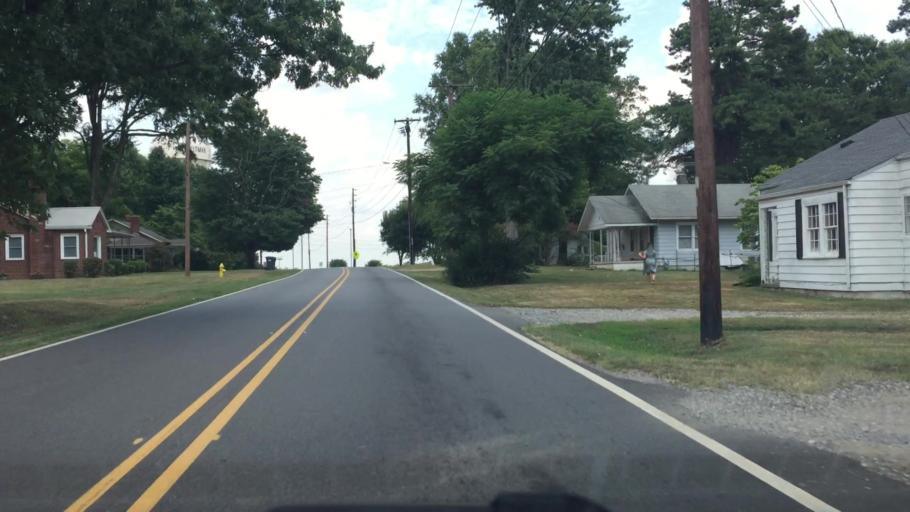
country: US
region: North Carolina
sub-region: Iredell County
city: Troutman
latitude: 35.7113
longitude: -80.8929
